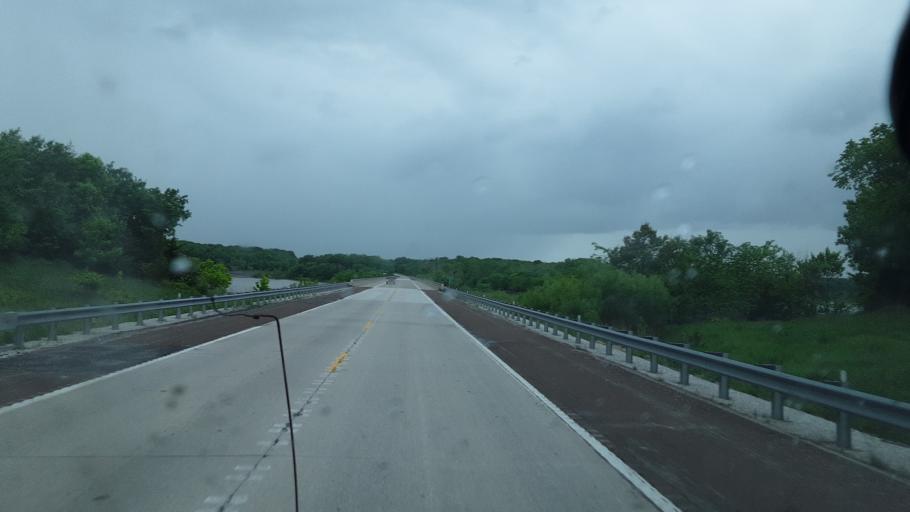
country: US
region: Missouri
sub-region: Monroe County
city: Paris
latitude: 39.5377
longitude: -91.8989
